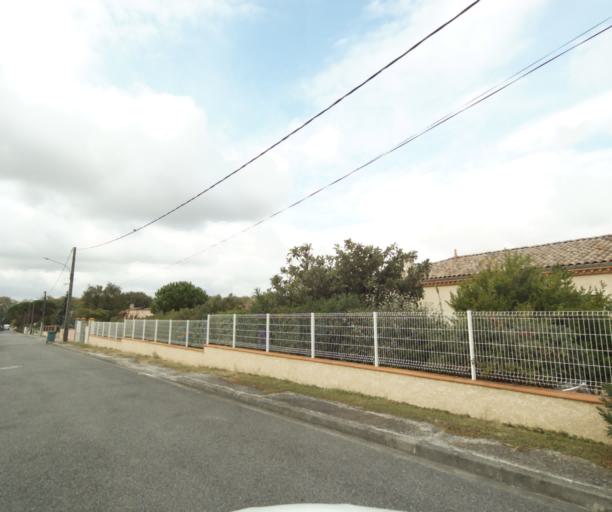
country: FR
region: Midi-Pyrenees
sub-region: Departement de la Haute-Garonne
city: Villefranche-de-Lauragais
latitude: 43.4119
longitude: 1.7097
